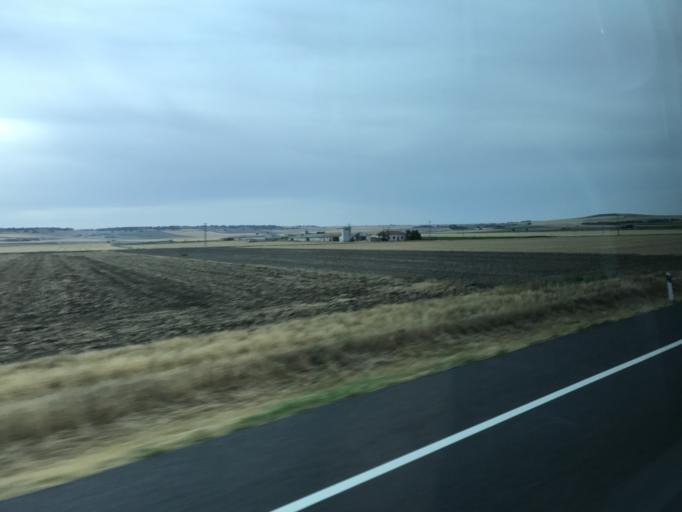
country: ES
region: Castille and Leon
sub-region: Provincia de Segovia
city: Tolocirio
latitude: 41.1397
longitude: -4.6489
